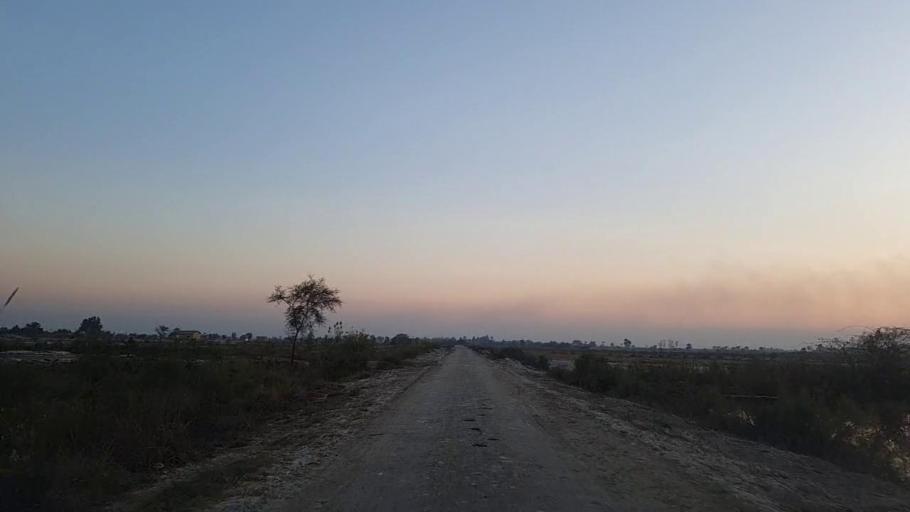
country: PK
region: Sindh
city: Bandhi
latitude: 26.5935
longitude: 68.3360
